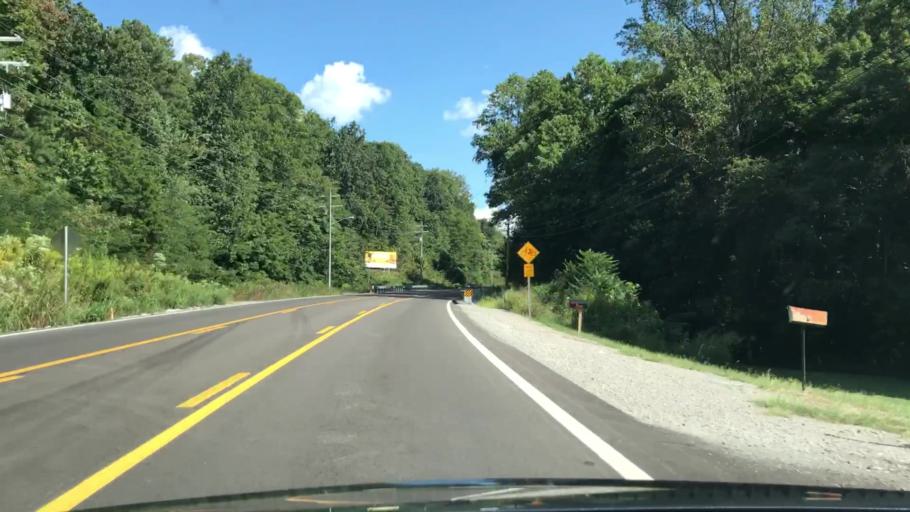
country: US
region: Alabama
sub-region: Limestone County
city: Ardmore
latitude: 35.0042
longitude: -86.8708
